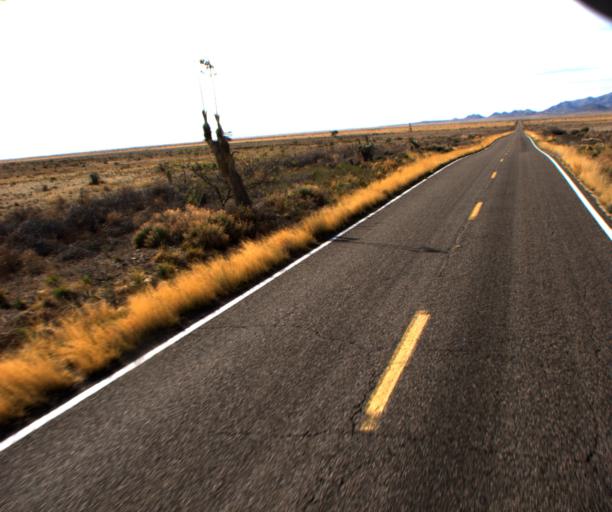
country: US
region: Arizona
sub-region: Cochise County
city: Willcox
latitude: 32.0661
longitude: -109.5069
